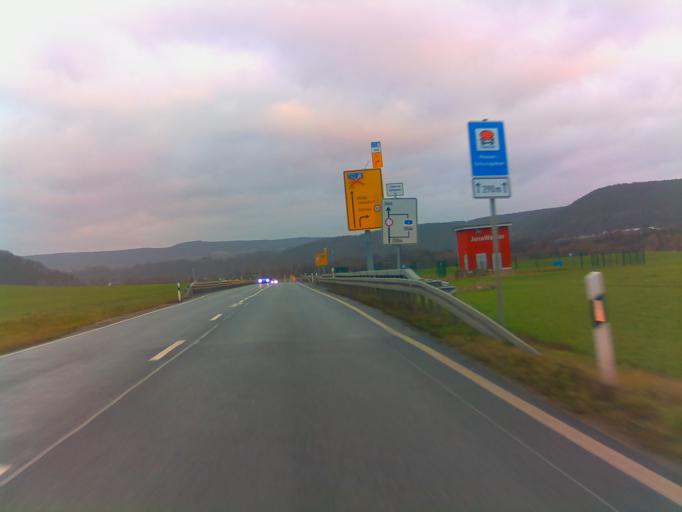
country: DE
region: Thuringia
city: Schops
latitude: 50.8276
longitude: 11.5891
